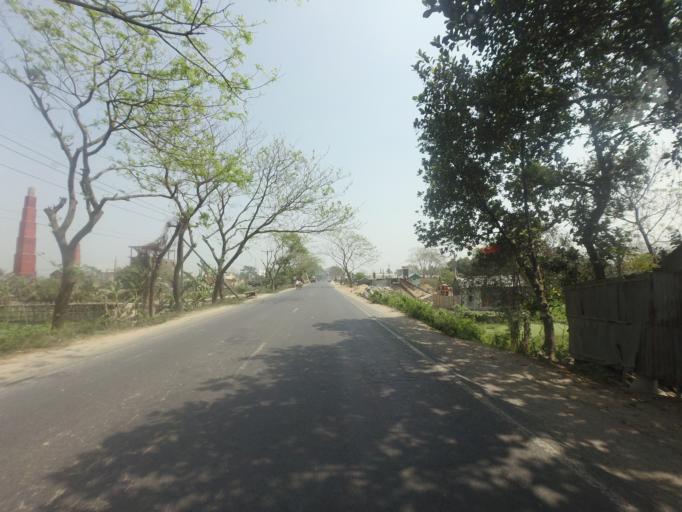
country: BD
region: Dhaka
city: Bhairab Bazar
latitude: 24.0419
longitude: 91.0454
